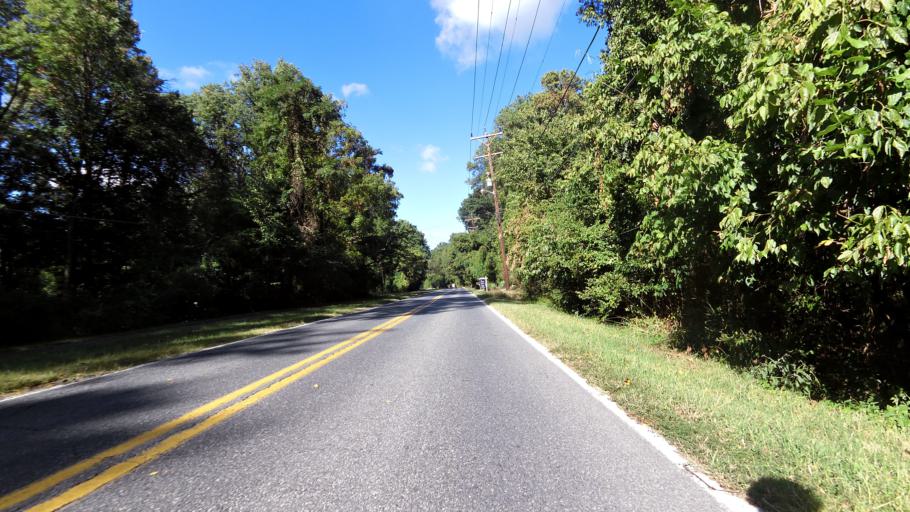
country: US
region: Maryland
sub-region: Montgomery County
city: Cabin John
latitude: 38.9760
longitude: -77.1801
